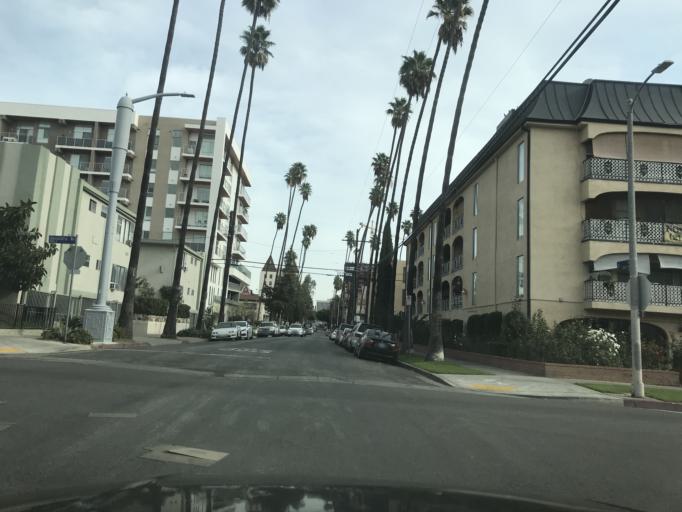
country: US
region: California
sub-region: Los Angeles County
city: Silver Lake
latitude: 34.0654
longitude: -118.2981
